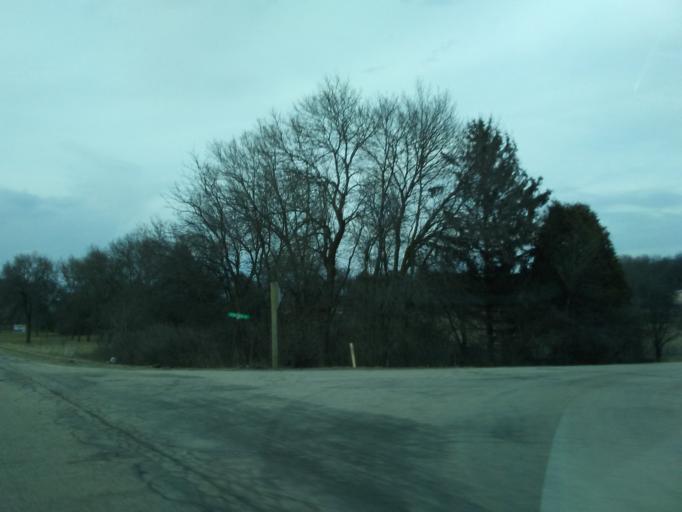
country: US
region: Wisconsin
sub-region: Dane County
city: Verona
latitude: 43.0097
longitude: -89.5336
